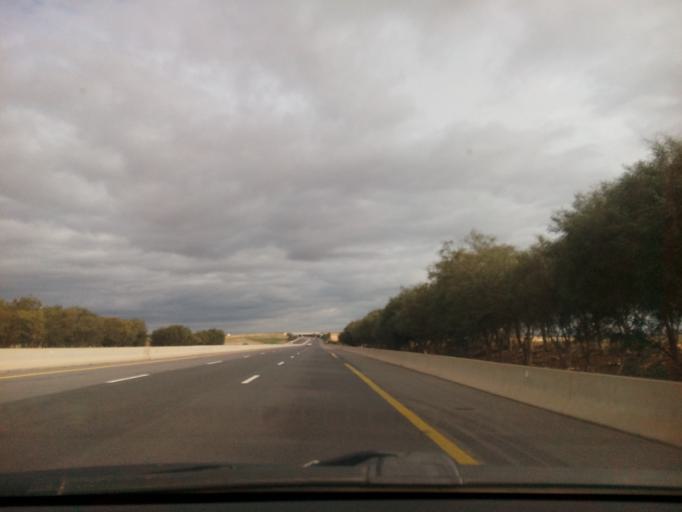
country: DZ
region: Sidi Bel Abbes
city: Sidi Bel Abbes
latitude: 35.1872
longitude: -0.7193
